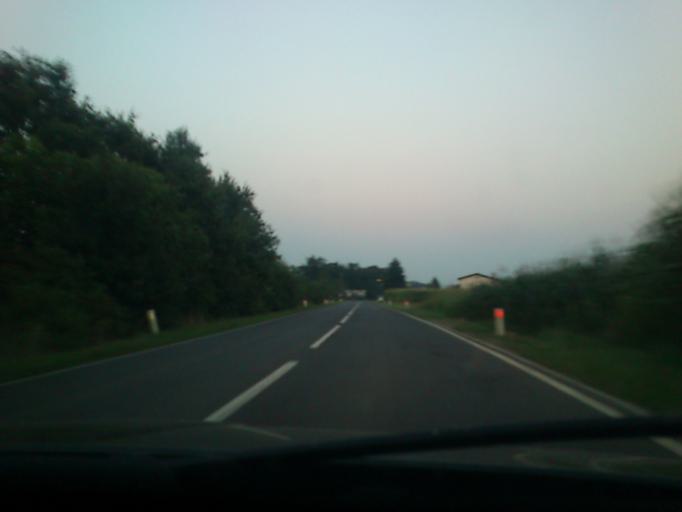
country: SI
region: Duplek
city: Zgornji Duplek
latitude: 46.4913
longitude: 15.7215
